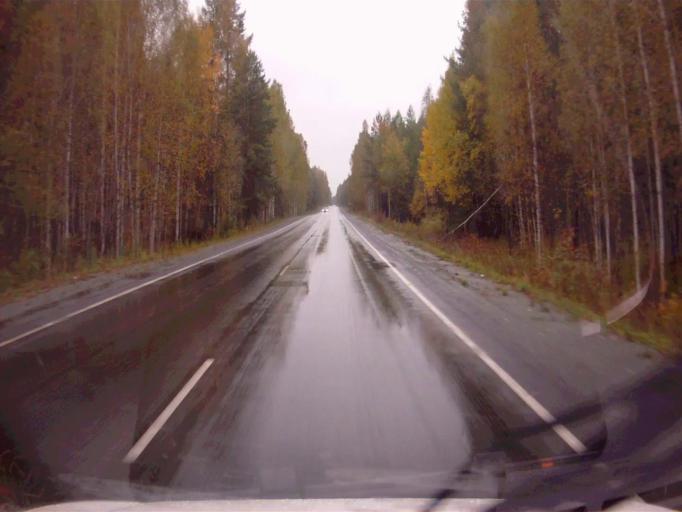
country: RU
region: Chelyabinsk
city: Tayginka
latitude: 55.5805
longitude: 60.6411
